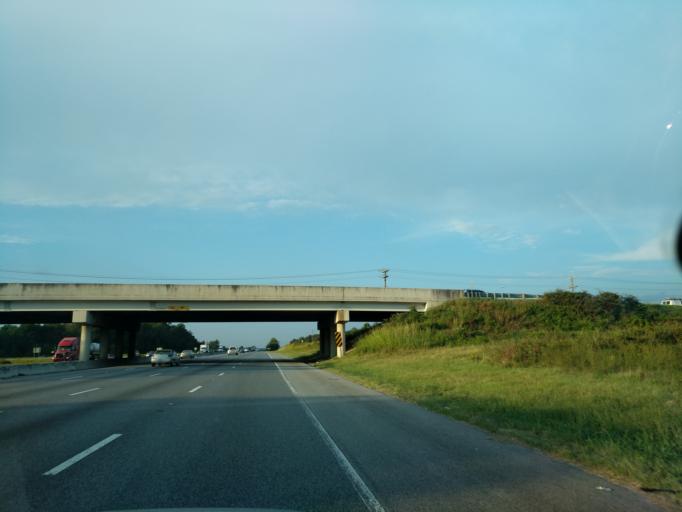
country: US
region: South Carolina
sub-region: Anderson County
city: Piedmont
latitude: 34.7091
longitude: -82.4996
